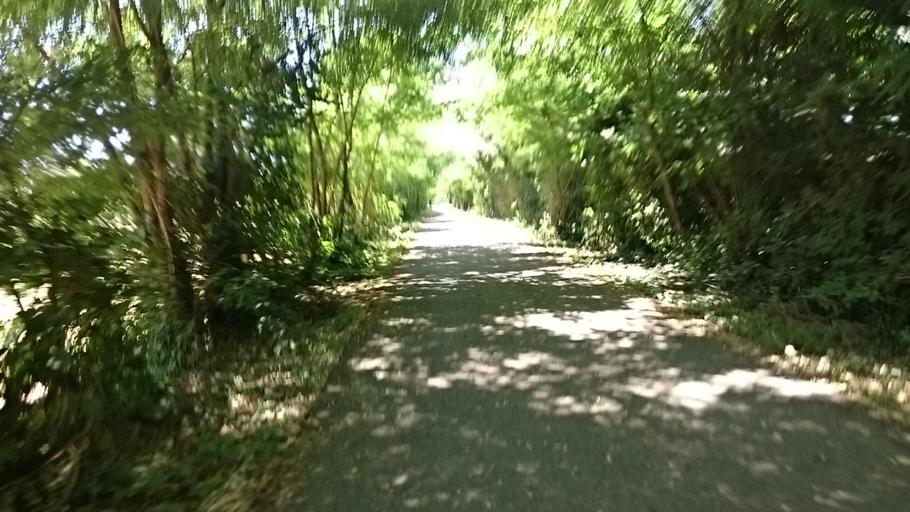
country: IT
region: Veneto
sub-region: Provincia di Padova
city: Trebaseleghe
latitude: 45.6167
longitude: 12.0507
